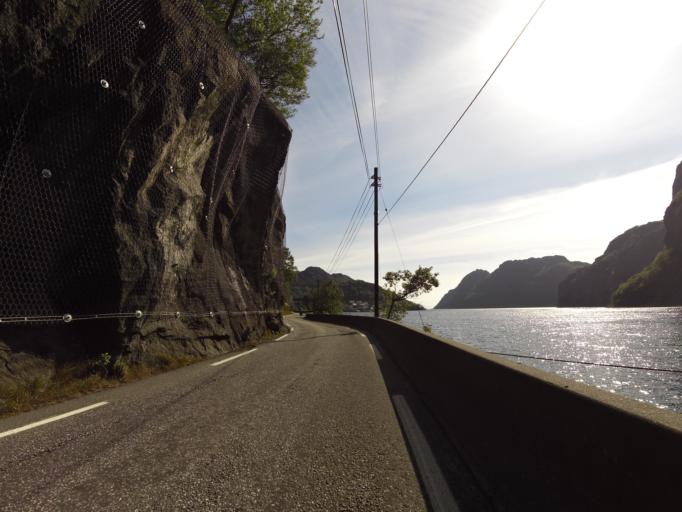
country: NO
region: Rogaland
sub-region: Sokndal
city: Hauge i Dalane
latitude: 58.3232
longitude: 6.3514
